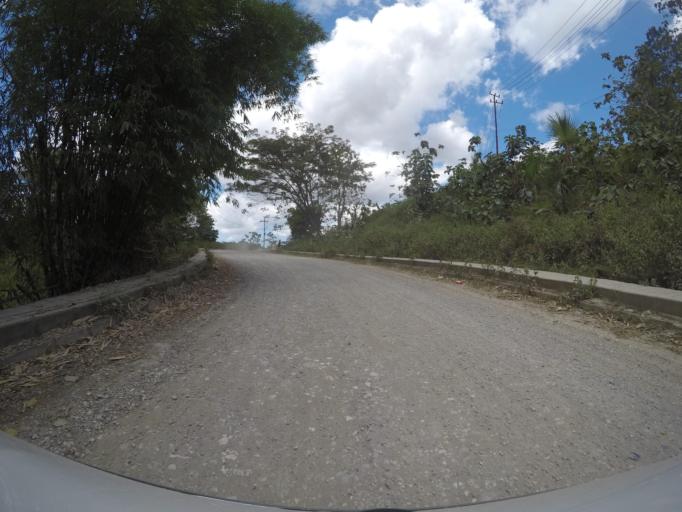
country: TL
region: Viqueque
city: Viqueque
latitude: -8.8457
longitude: 126.3692
